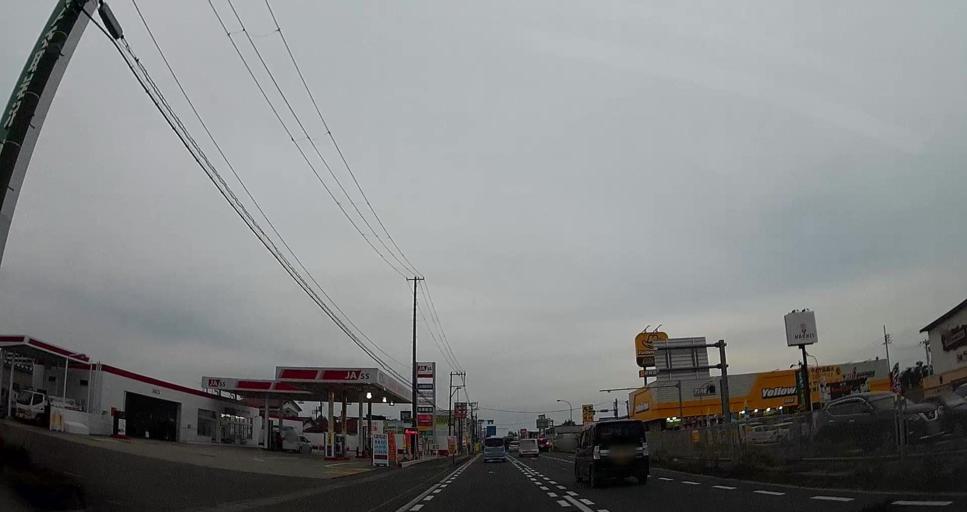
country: JP
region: Miyagi
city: Iwanuma
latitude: 38.1682
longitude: 140.8899
